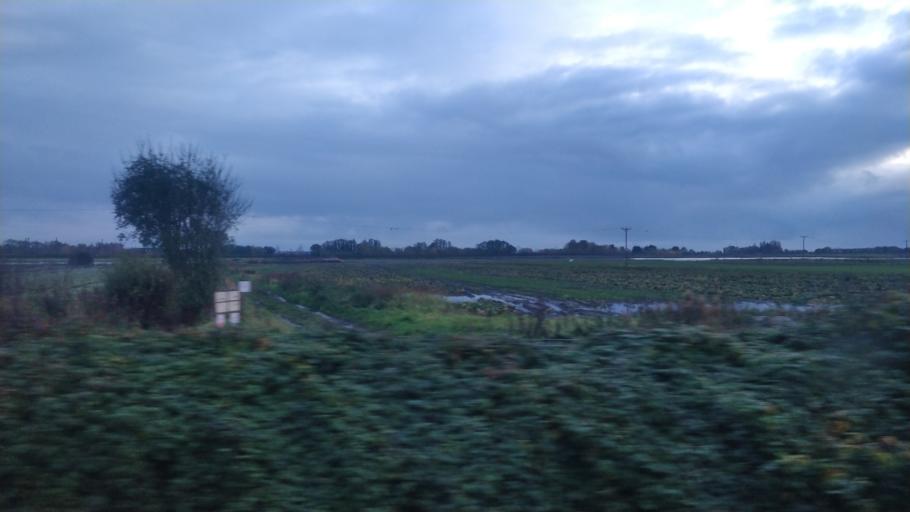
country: GB
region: England
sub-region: Lancashire
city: Ormskirk
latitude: 53.6126
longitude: -2.8708
